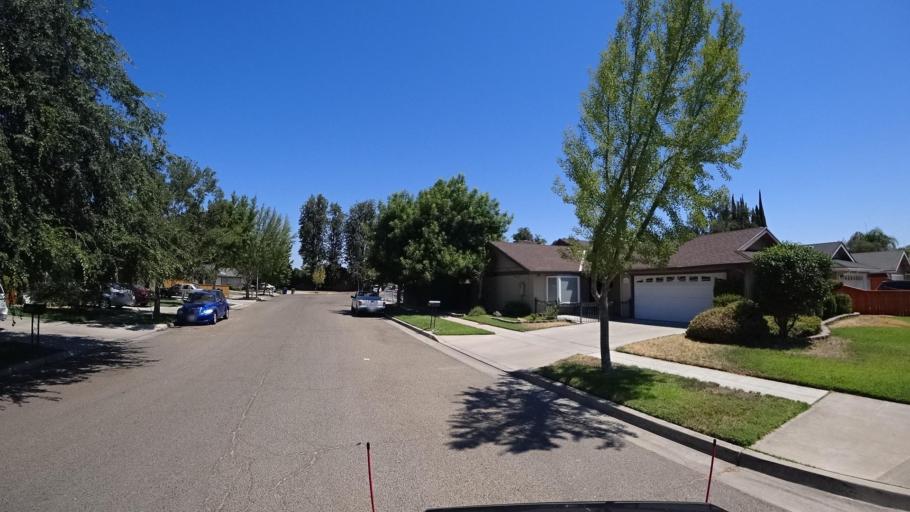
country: US
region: California
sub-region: Fresno County
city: Sunnyside
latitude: 36.7687
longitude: -119.7345
